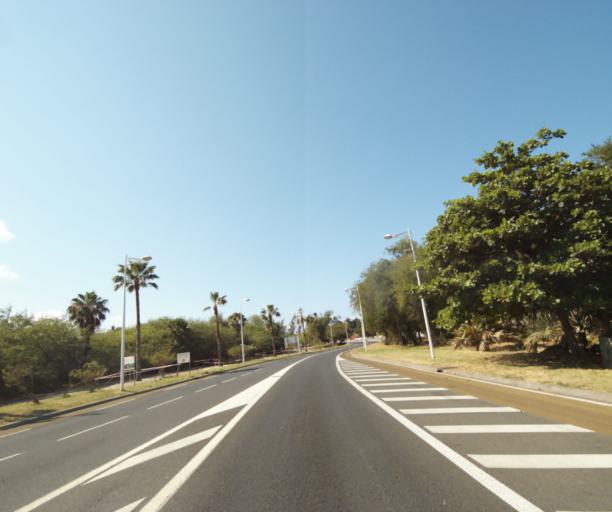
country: RE
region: Reunion
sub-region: Reunion
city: Trois-Bassins
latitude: -21.0754
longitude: 55.2281
